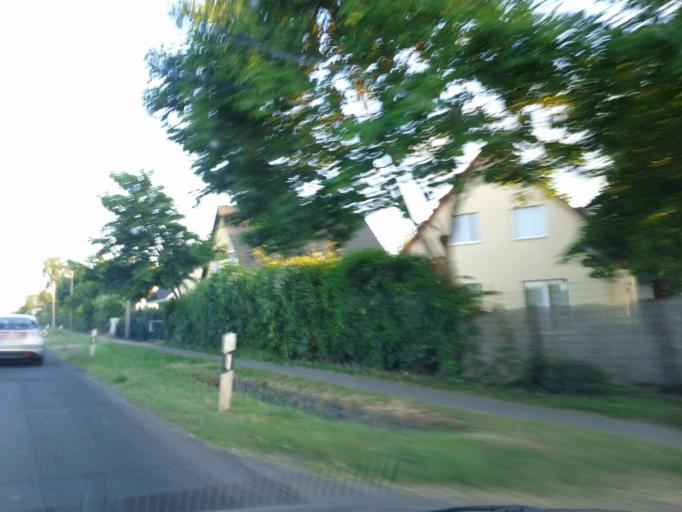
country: DE
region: Brandenburg
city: Hoppegarten
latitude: 52.5249
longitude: 13.6451
